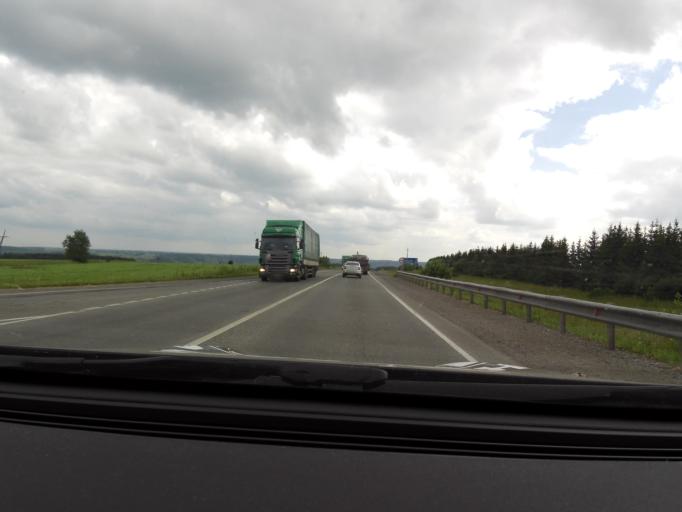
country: RU
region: Perm
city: Kungur
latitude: 57.4011
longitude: 56.8938
